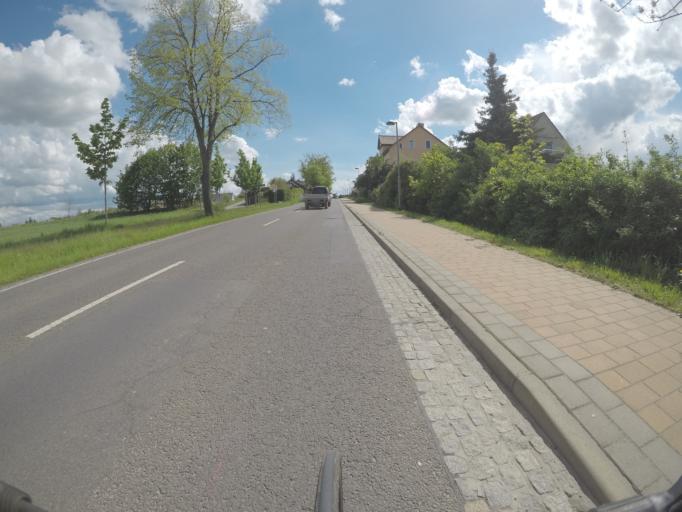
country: DE
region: Brandenburg
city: Bernau bei Berlin
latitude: 52.6916
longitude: 13.5884
